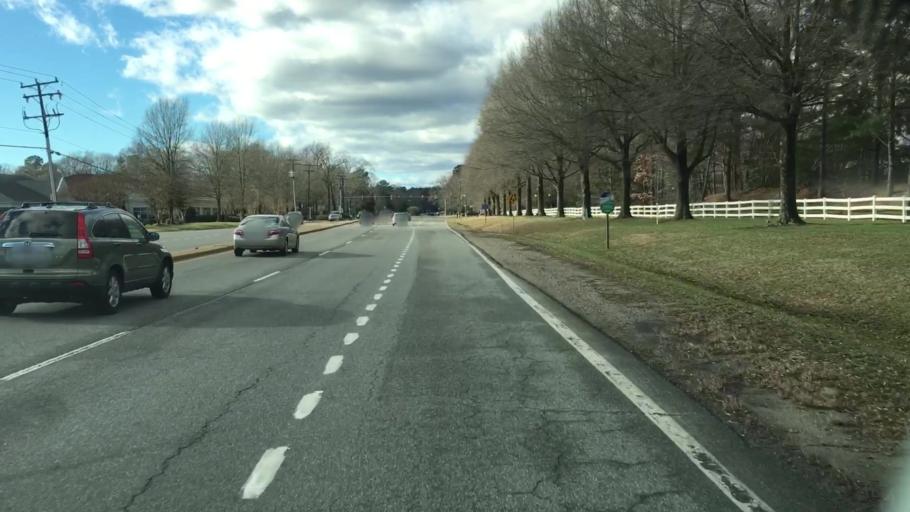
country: US
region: Virginia
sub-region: Chesterfield County
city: Bon Air
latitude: 37.5227
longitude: -77.6129
